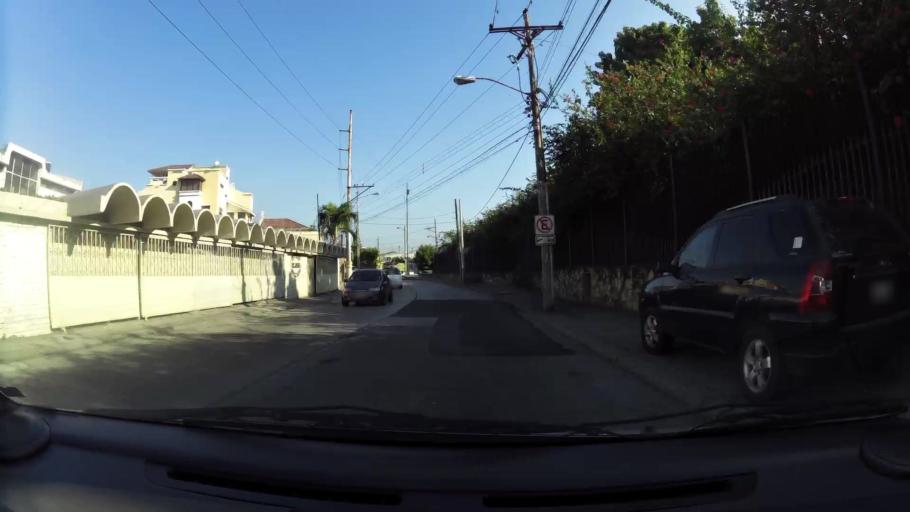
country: EC
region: Guayas
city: Guayaquil
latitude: -2.1650
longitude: -79.9061
